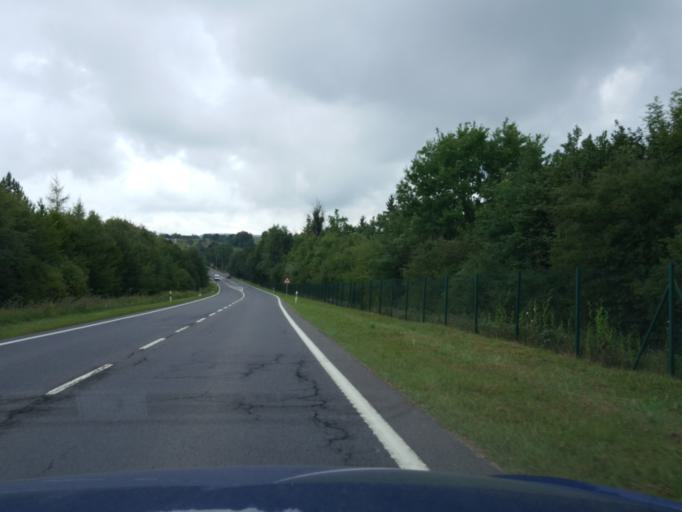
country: LU
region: Luxembourg
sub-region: Canton de Mersch
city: Bissen
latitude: 49.7693
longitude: 6.0868
